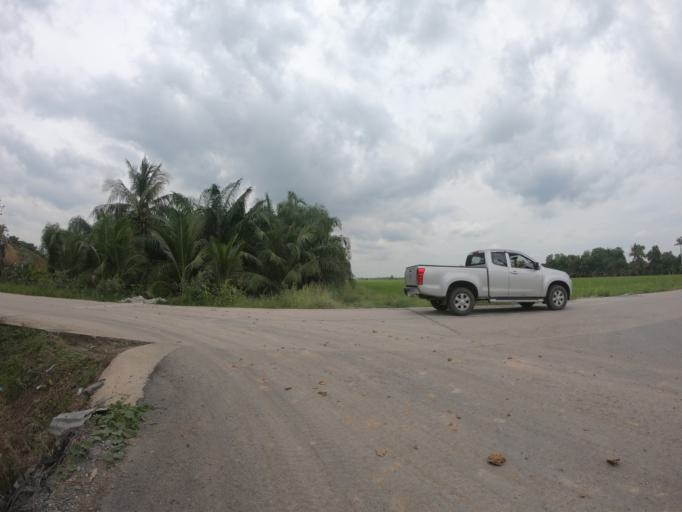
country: TH
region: Pathum Thani
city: Ban Lam Luk Ka
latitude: 14.0343
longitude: 100.8663
